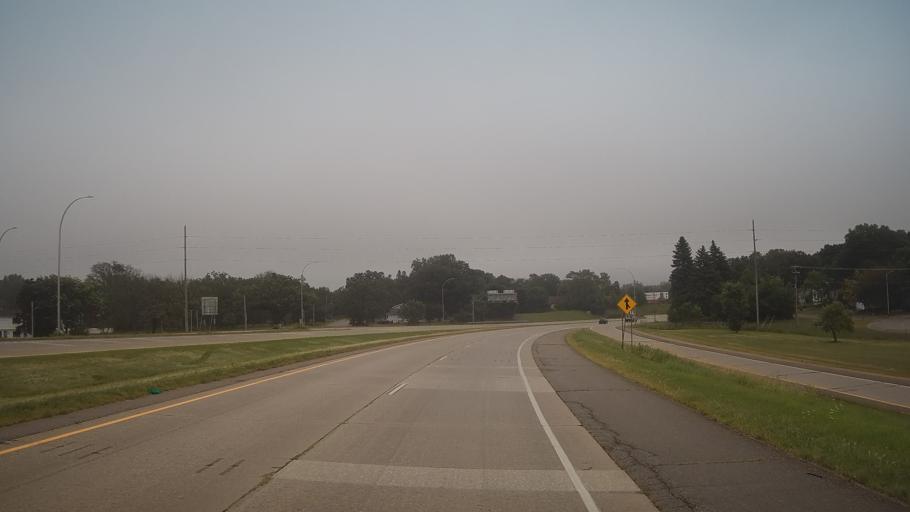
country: US
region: Minnesota
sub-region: Mower County
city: Austin
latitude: 43.6805
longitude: -92.9664
